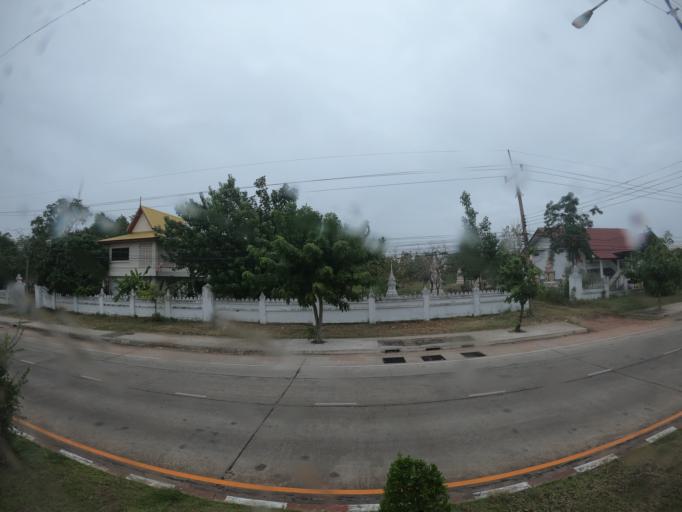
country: TH
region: Maha Sarakham
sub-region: Amphoe Borabue
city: Borabue
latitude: 16.0371
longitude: 103.1243
